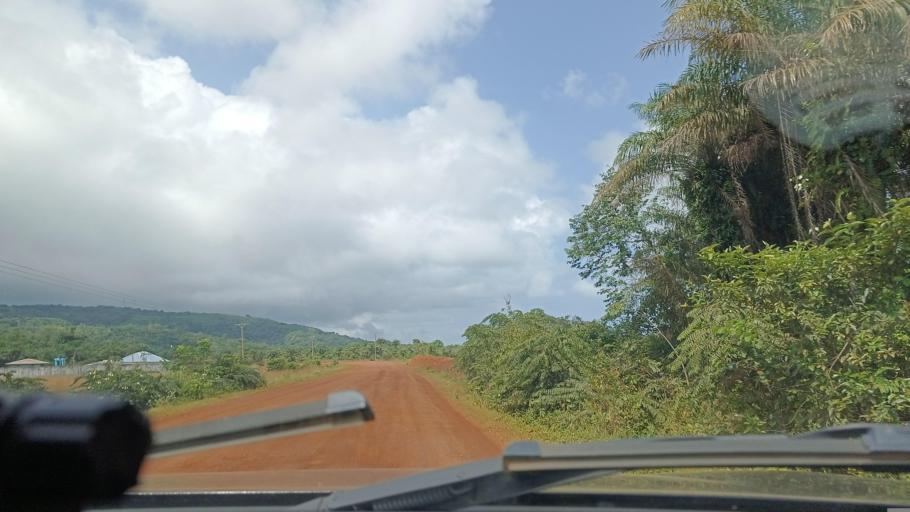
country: LR
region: Grand Cape Mount
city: Robertsport
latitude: 6.7466
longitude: -11.3449
